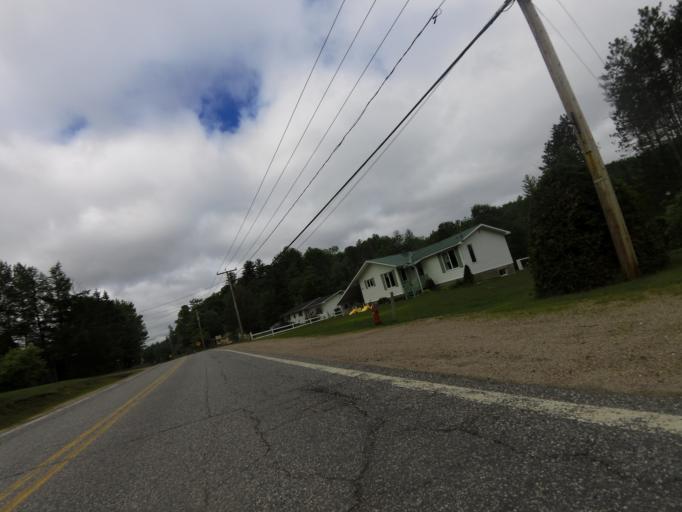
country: CA
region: Quebec
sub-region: Outaouais
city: Shawville
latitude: 45.8402
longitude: -76.4417
